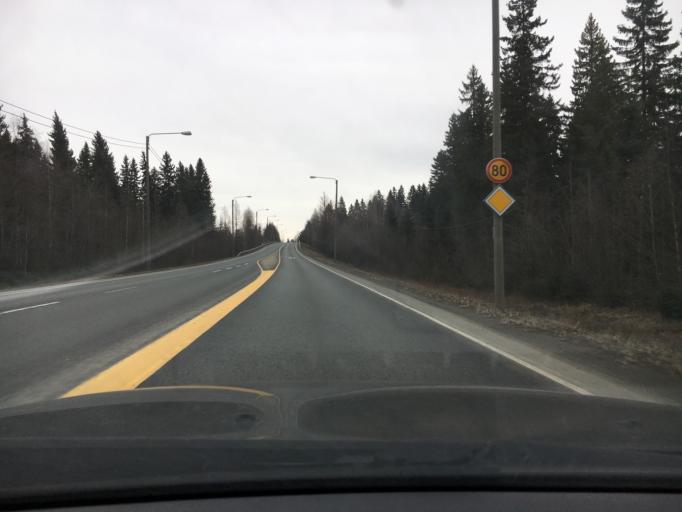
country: FI
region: Northern Savo
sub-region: Kuopio
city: Siilinjaervi
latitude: 63.0865
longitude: 27.6489
